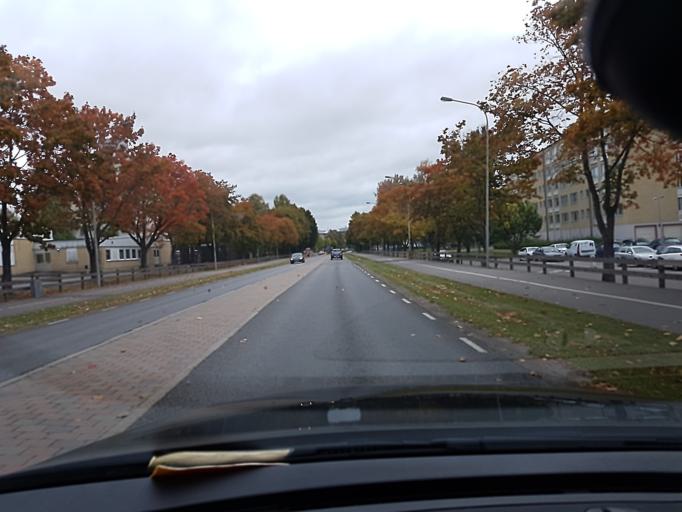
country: SE
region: Kronoberg
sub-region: Vaxjo Kommun
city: Vaexjoe
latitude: 56.8885
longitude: 14.7998
